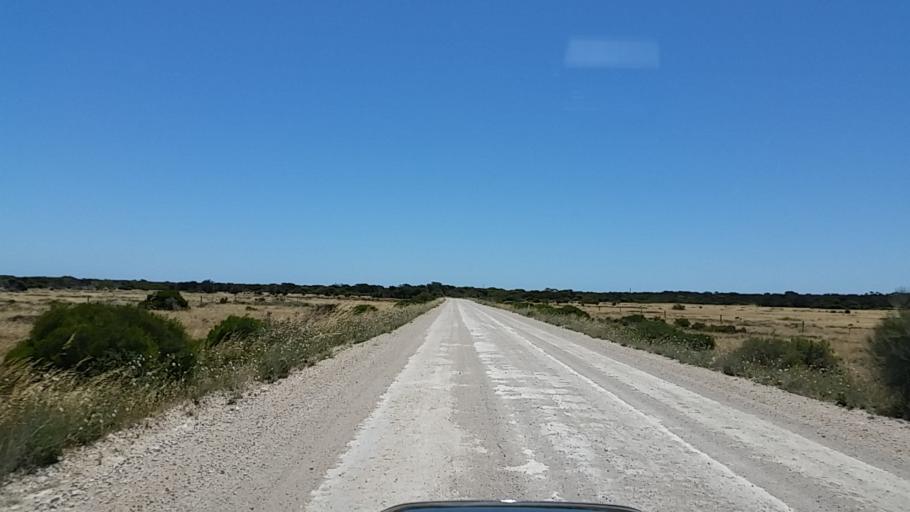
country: AU
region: South Australia
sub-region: Yorke Peninsula
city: Honiton
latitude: -35.2150
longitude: 137.0424
